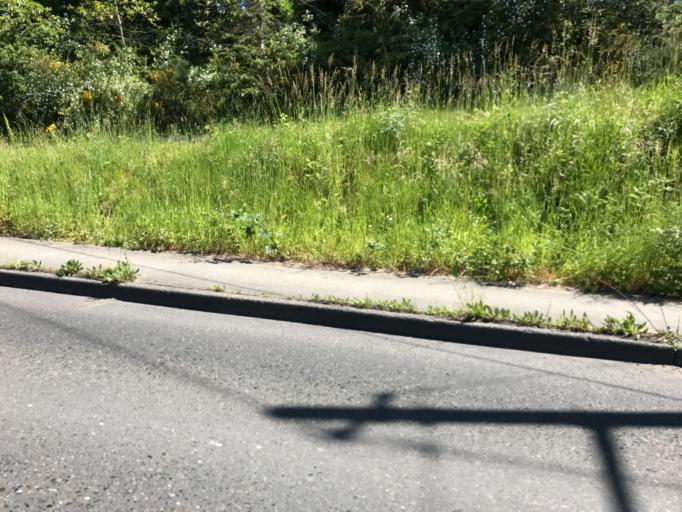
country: US
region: Washington
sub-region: King County
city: Seattle
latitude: 47.5817
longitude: -122.2972
